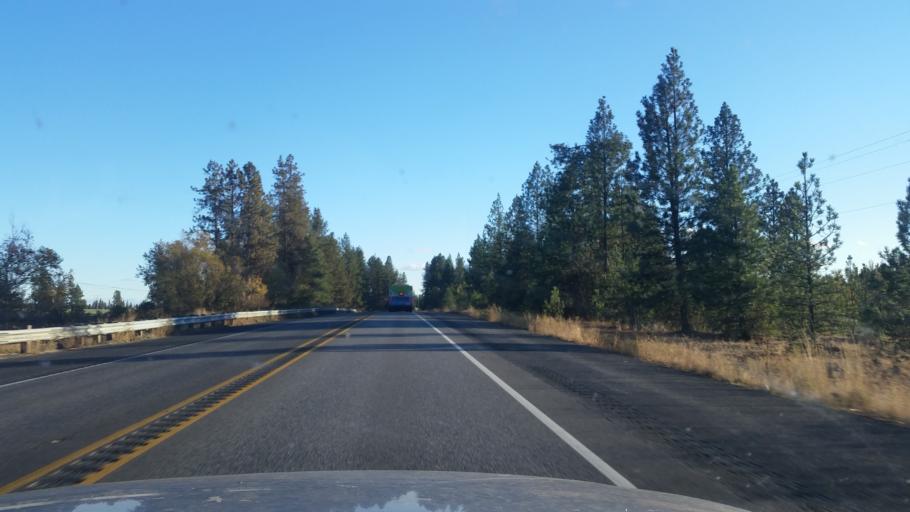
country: US
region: Washington
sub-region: Spokane County
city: Cheney
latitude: 47.5217
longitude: -117.5655
